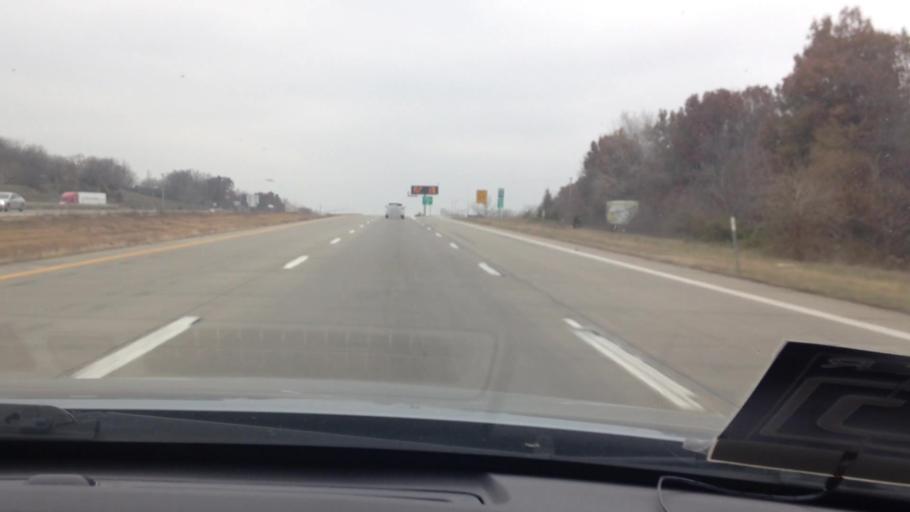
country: US
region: Missouri
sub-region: Cass County
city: Harrisonville
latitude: 38.6247
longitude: -94.3495
